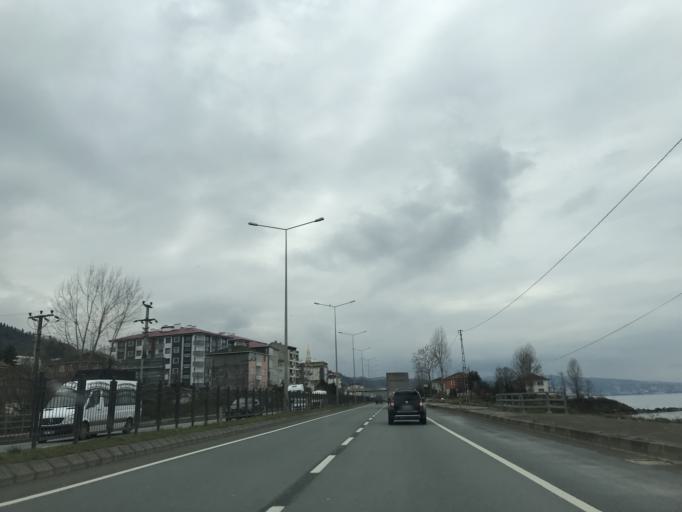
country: TR
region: Trabzon
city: Arsin
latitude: 40.9590
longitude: 39.9554
